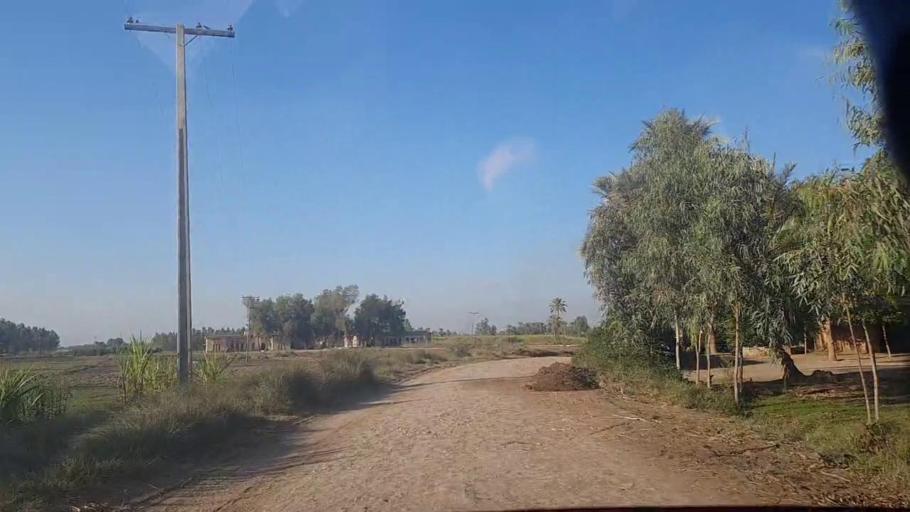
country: PK
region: Sindh
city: Sobhadero
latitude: 27.3960
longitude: 68.4195
